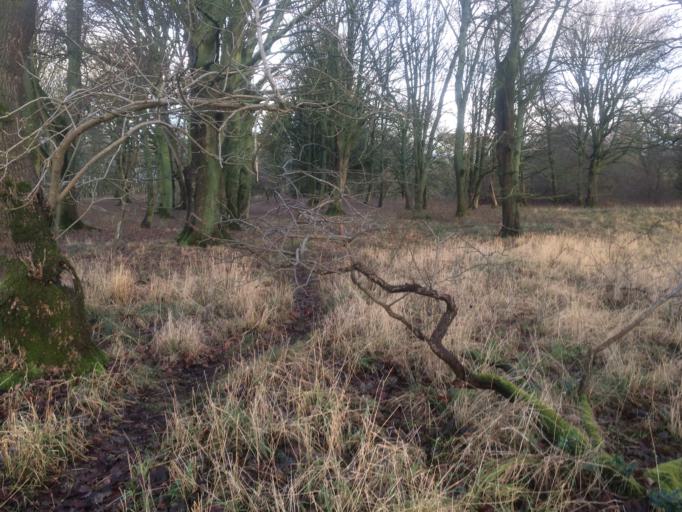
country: GB
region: Scotland
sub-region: Midlothian
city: Loanhead
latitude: 55.8611
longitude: -3.1457
